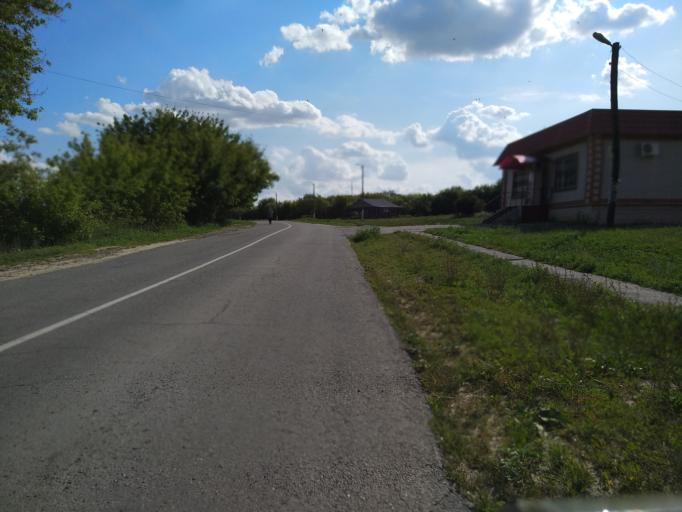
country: RU
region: Lipetsk
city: Dobrinka
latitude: 52.0402
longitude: 40.5547
